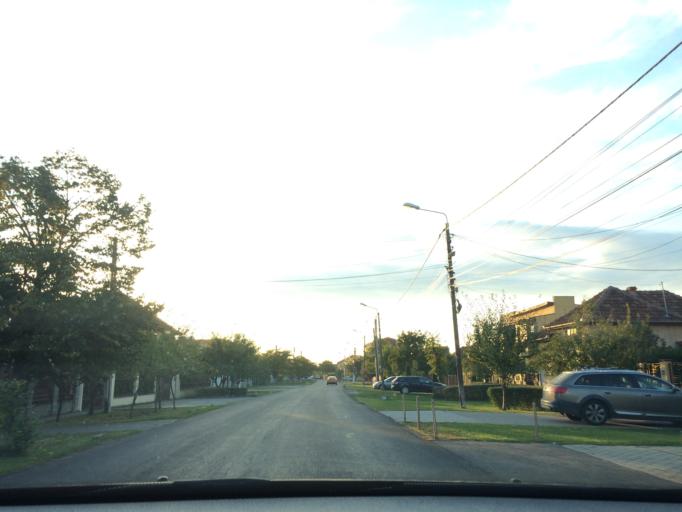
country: RO
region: Timis
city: Timisoara
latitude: 45.7630
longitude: 21.1921
